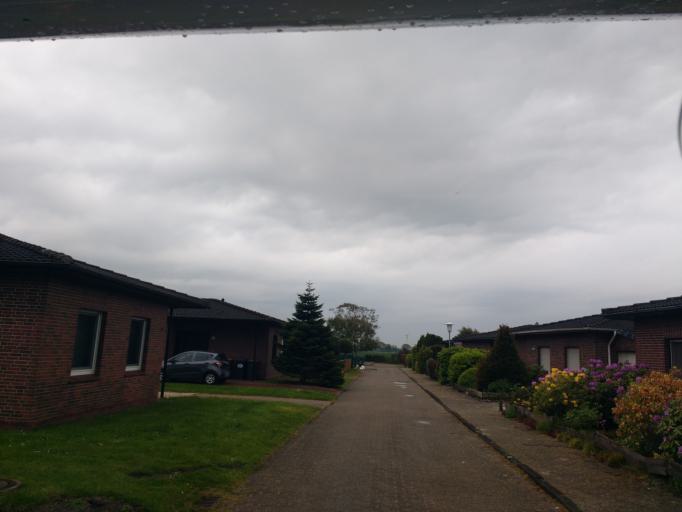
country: DE
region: Lower Saxony
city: Schillig
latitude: 53.7060
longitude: 8.0168
